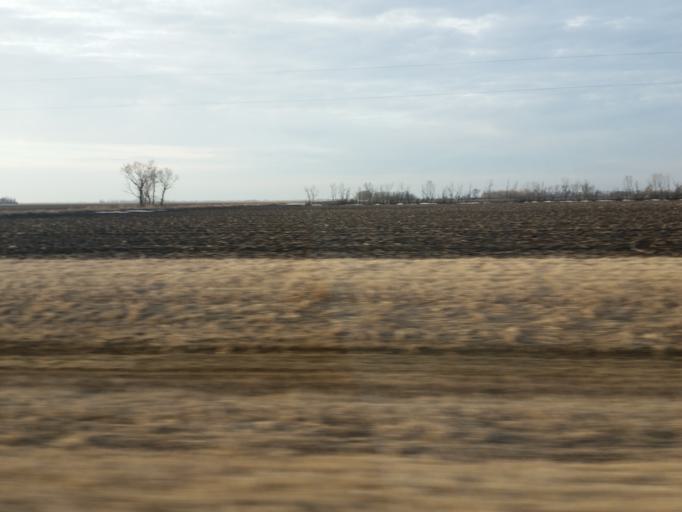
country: US
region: North Dakota
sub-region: Traill County
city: Mayville
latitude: 47.3529
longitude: -97.2717
